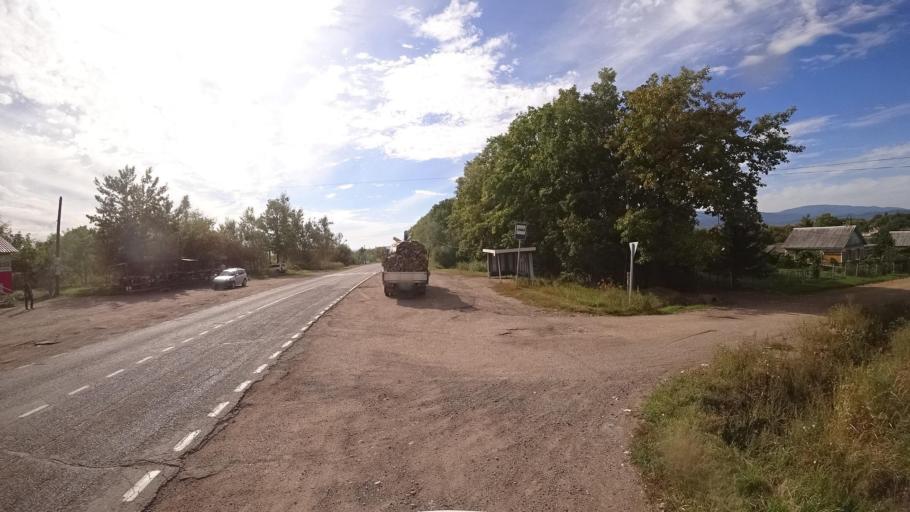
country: RU
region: Primorskiy
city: Dostoyevka
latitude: 44.3220
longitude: 133.4839
